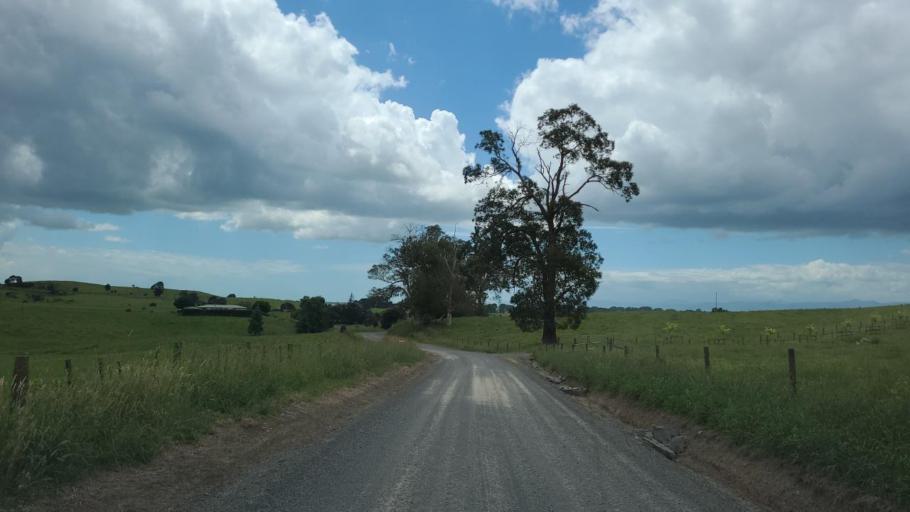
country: NZ
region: Waikato
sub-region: Hauraki District
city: Ngatea
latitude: -37.4544
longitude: 175.5007
